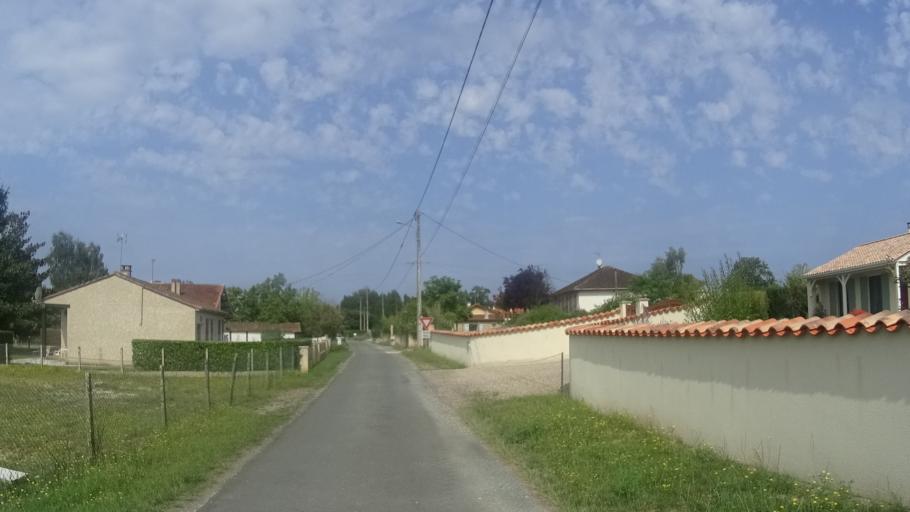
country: FR
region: Aquitaine
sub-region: Departement de la Dordogne
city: Sourzac
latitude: 45.0556
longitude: 0.3978
